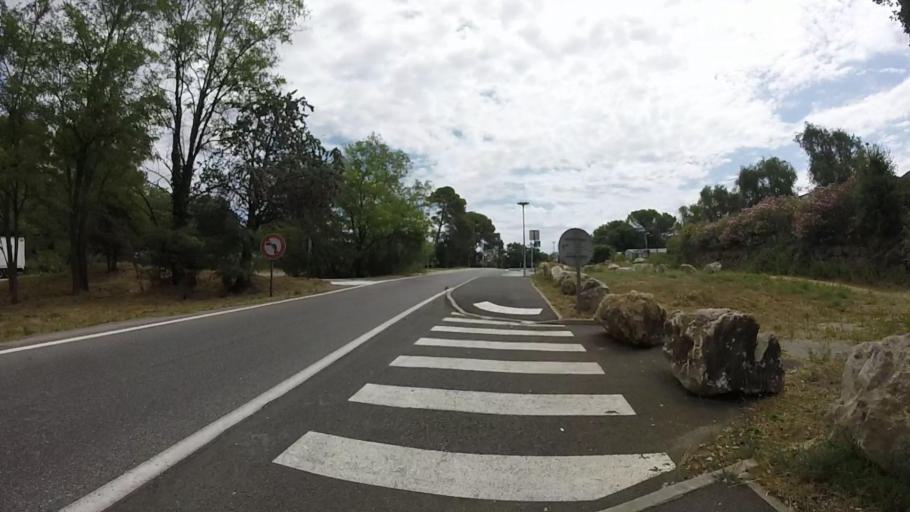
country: FR
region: Provence-Alpes-Cote d'Azur
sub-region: Departement des Alpes-Maritimes
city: Biot
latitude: 43.6152
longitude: 7.0851
